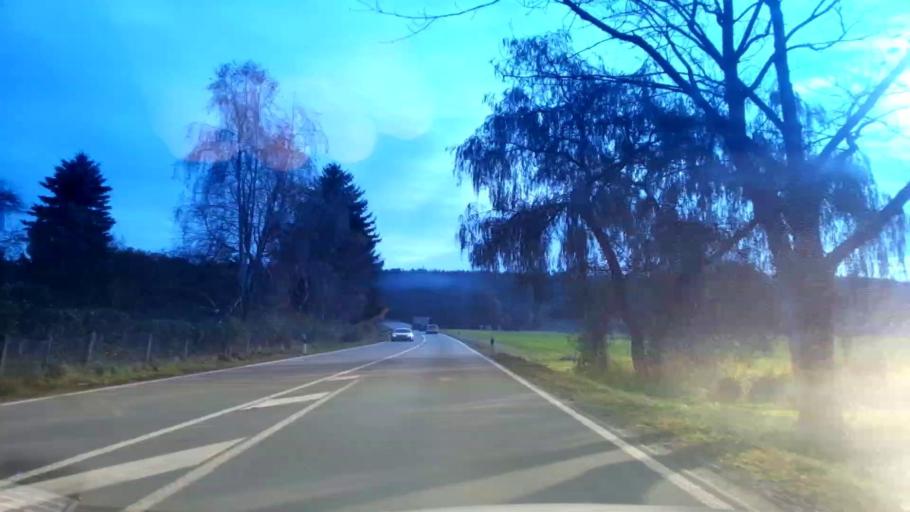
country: DE
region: Bavaria
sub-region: Upper Franconia
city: Kirchenpingarten
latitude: 49.9323
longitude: 11.7446
